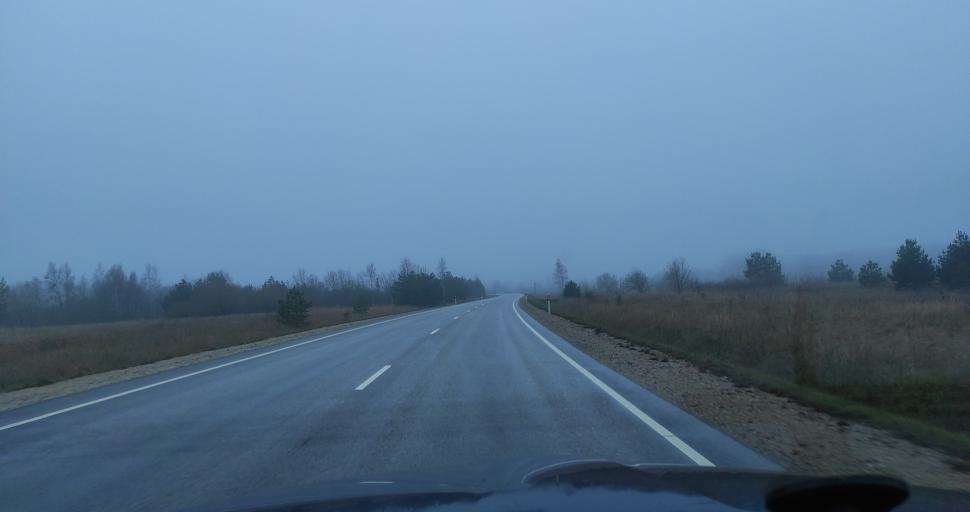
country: LV
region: Pavilostas
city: Pavilosta
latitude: 56.9321
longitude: 21.2728
